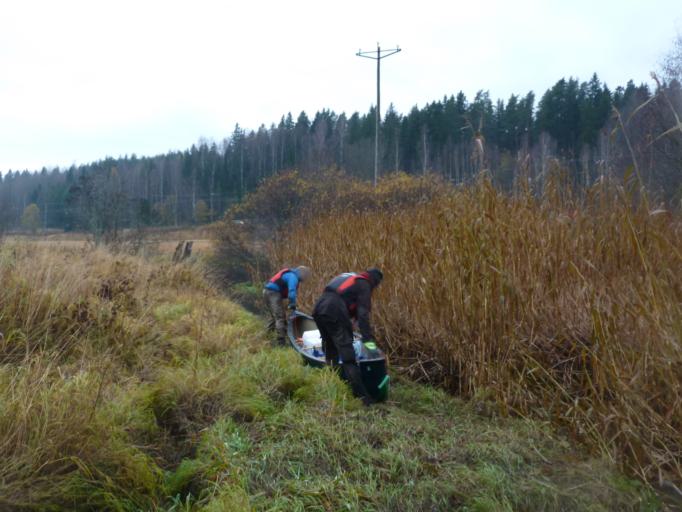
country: FI
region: Uusimaa
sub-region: Helsinki
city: Espoo
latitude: 60.1995
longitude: 24.6297
